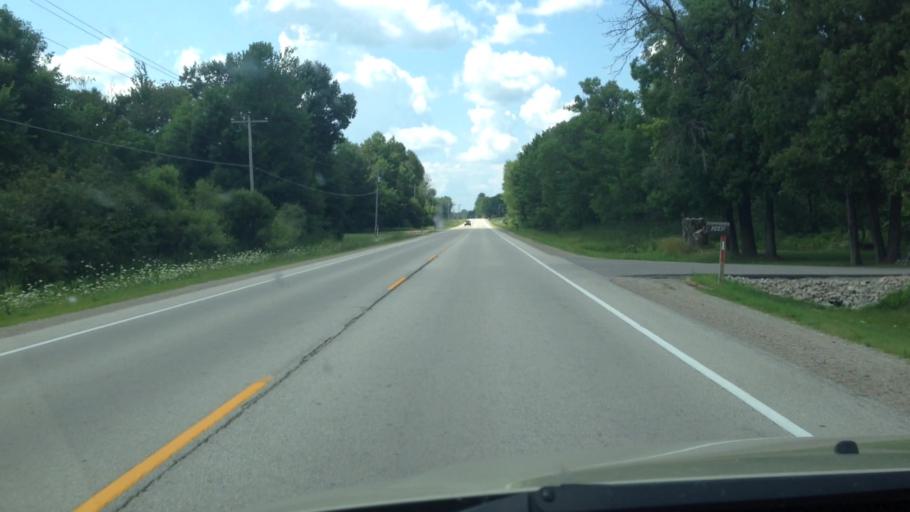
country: US
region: Wisconsin
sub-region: Brown County
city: Suamico
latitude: 44.6407
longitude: -88.0776
